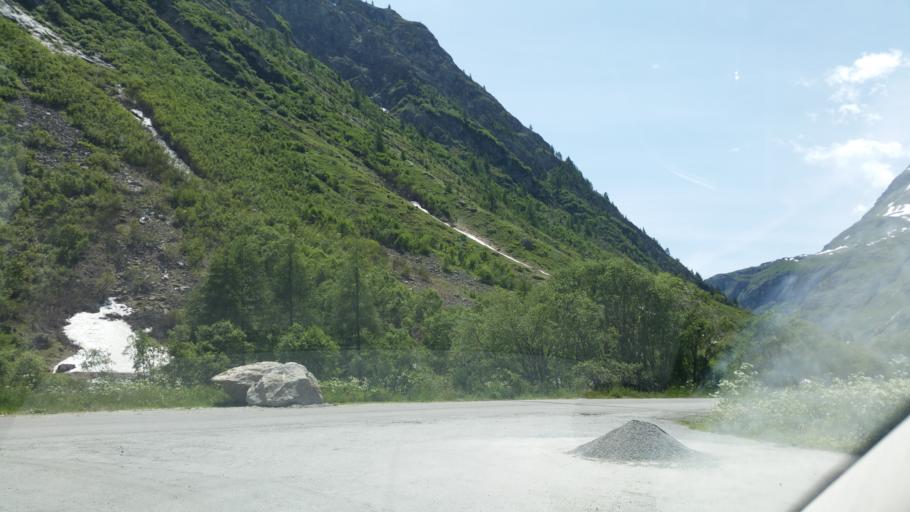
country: FR
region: Rhone-Alpes
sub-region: Departement de la Savoie
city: Val-d'Isere
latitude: 45.3706
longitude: 7.0466
